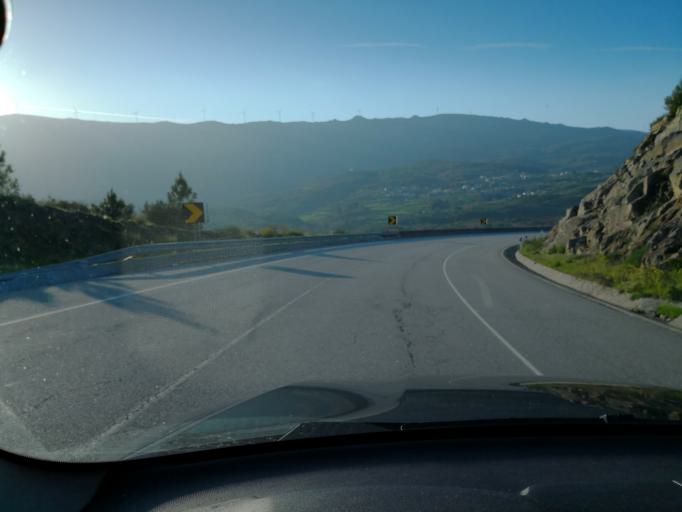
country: PT
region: Vila Real
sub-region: Vila Real
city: Vila Real
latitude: 41.3600
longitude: -7.7076
